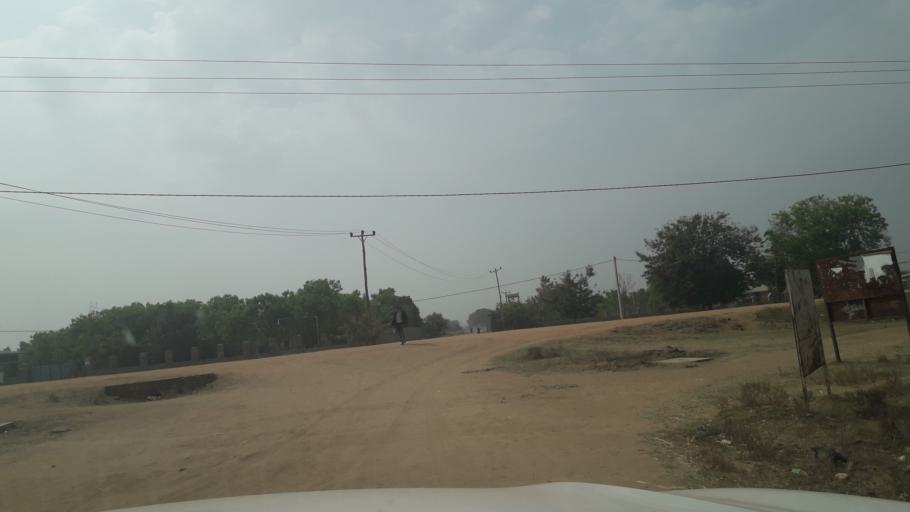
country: ET
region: Gambela
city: Gambela
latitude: 8.2984
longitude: 33.6826
